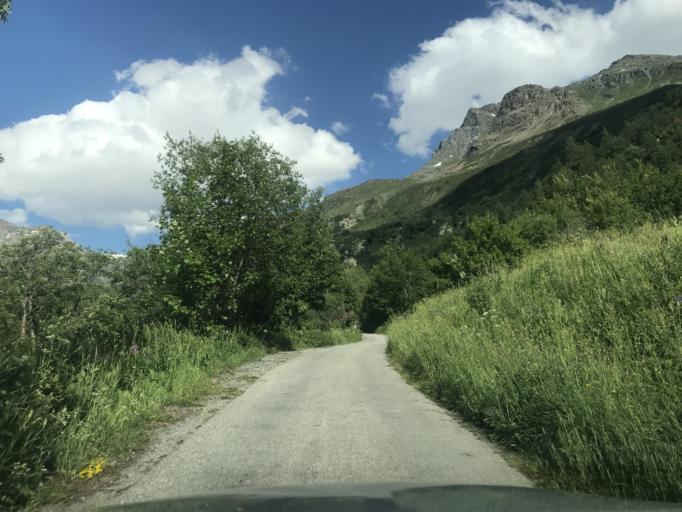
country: FR
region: Rhone-Alpes
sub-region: Departement de la Savoie
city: Val-d'Isere
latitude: 45.3734
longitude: 7.0631
